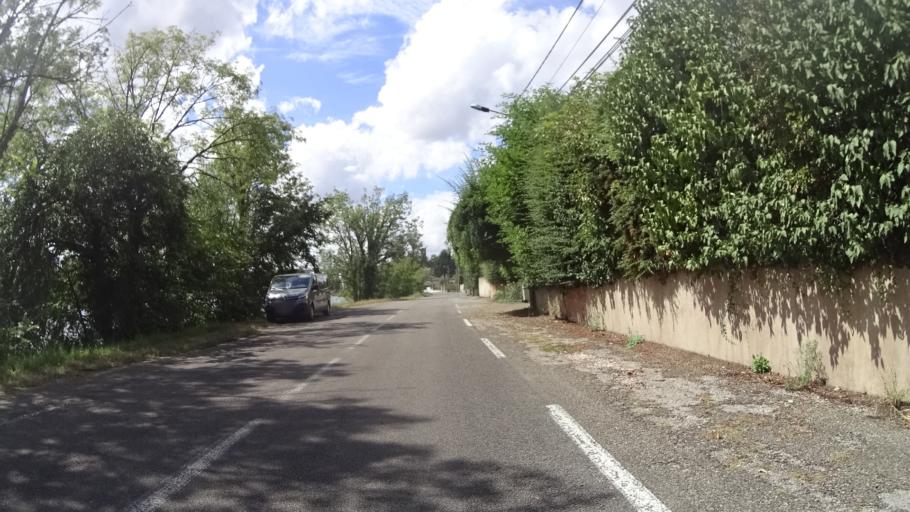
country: FR
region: Franche-Comte
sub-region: Departement du Jura
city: Dole
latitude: 47.0846
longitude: 5.4852
